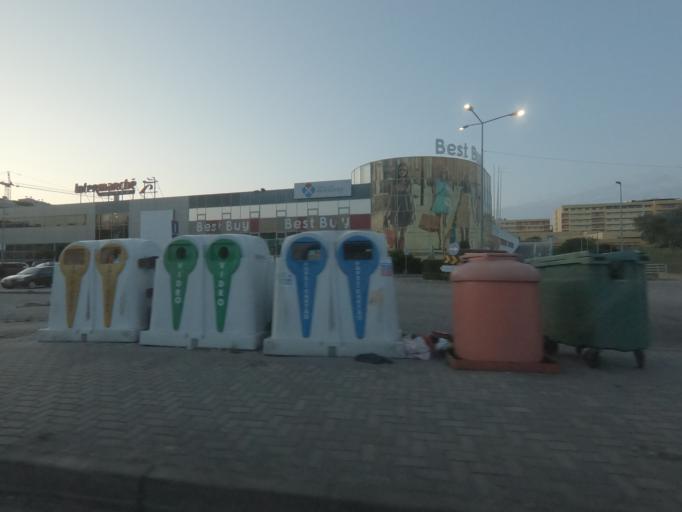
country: PT
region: Leiria
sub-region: Leiria
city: Leiria
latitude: 39.7411
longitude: -8.7959
